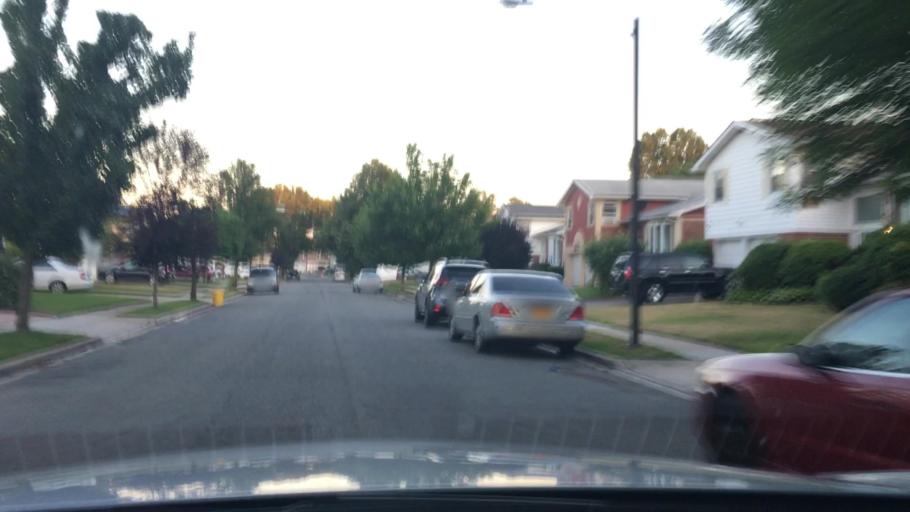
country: US
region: New York
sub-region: Nassau County
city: New Cassel
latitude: 40.7714
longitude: -73.5548
